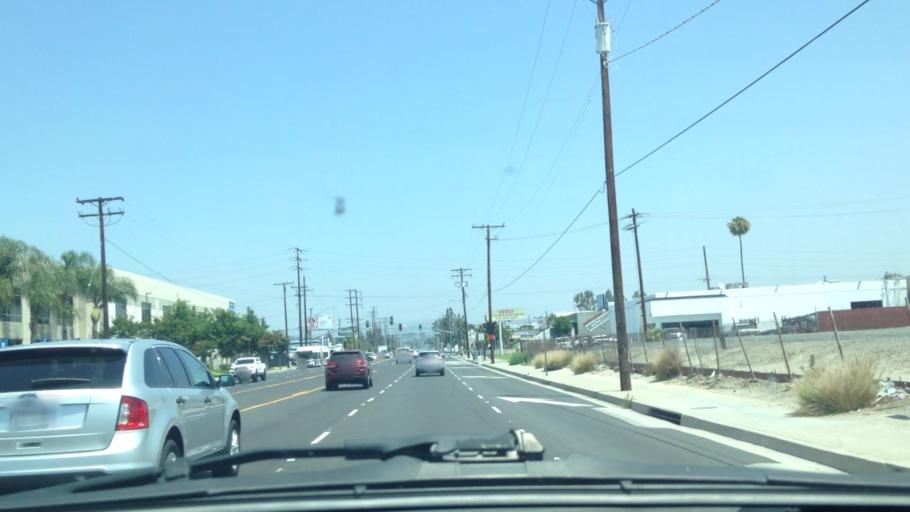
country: US
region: California
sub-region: Orange County
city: Placentia
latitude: 33.8579
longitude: -117.8893
